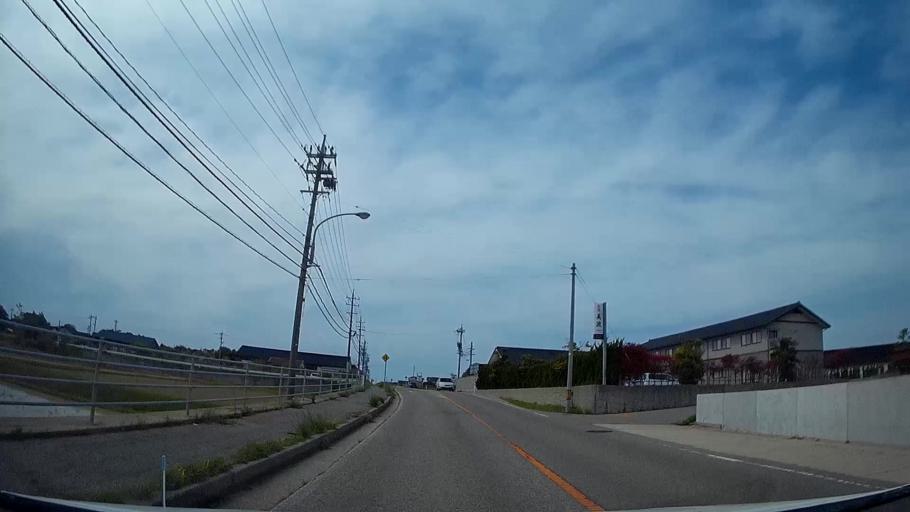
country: JP
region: Ishikawa
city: Hakui
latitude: 37.0102
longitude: 136.7629
